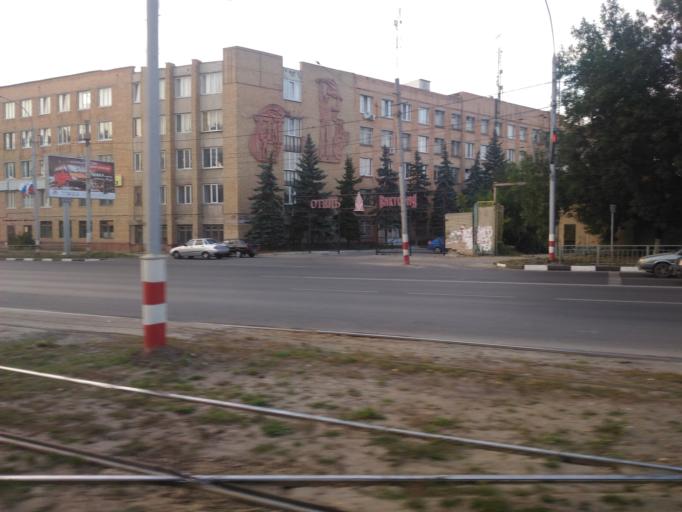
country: RU
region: Ulyanovsk
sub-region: Ulyanovskiy Rayon
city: Ulyanovsk
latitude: 54.3072
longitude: 48.3235
